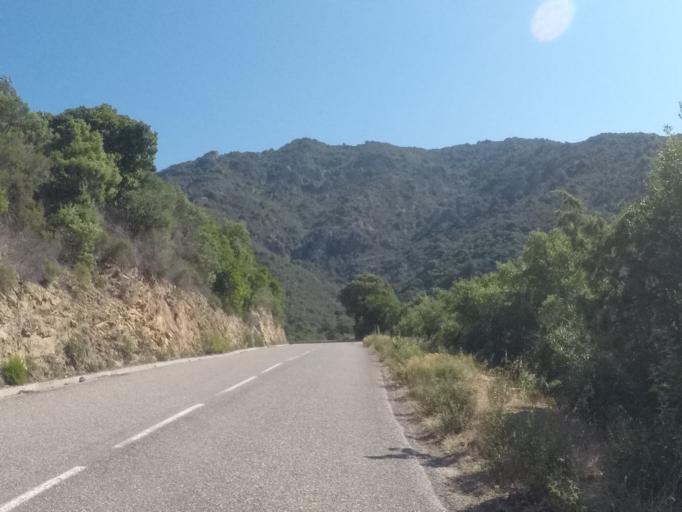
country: FR
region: Corsica
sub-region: Departement de la Haute-Corse
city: Calvi
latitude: 42.3716
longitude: 8.6693
